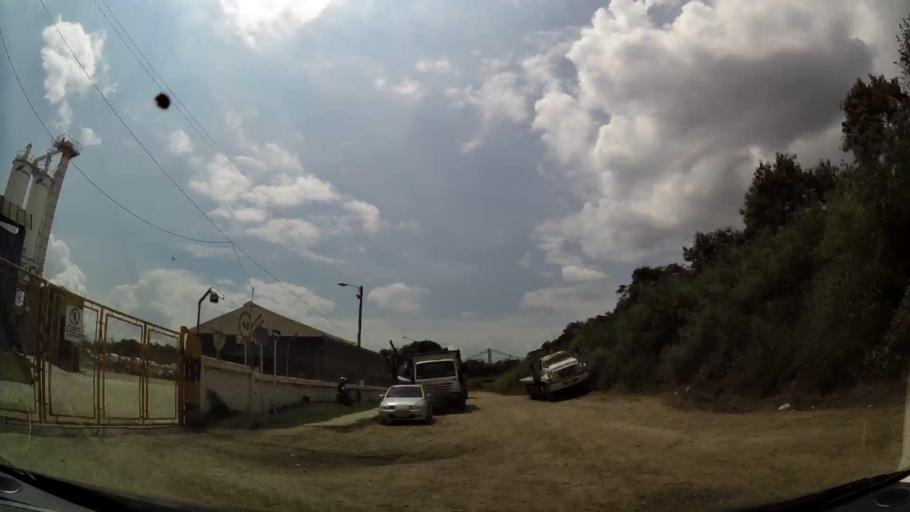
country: CO
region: Valle del Cauca
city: Cali
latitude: 3.4940
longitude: -76.4829
